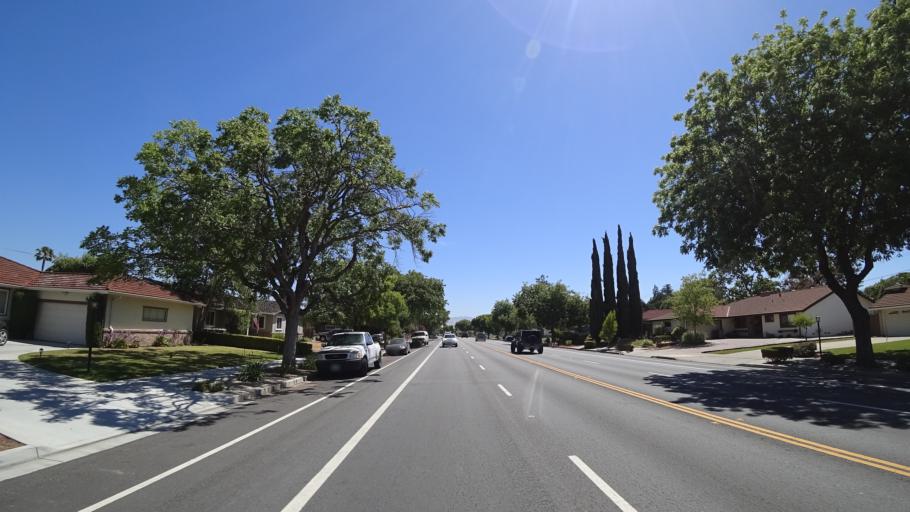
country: US
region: California
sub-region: Santa Clara County
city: Cambrian Park
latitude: 37.2730
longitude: -121.9306
